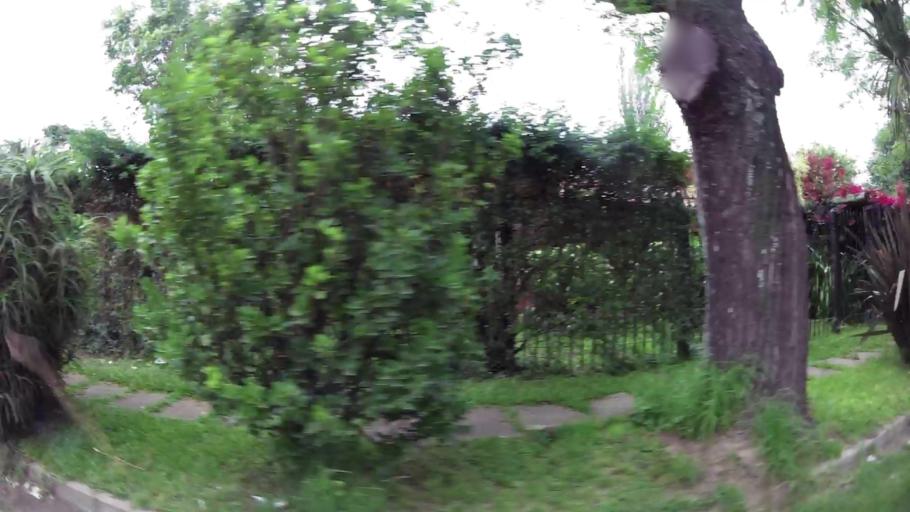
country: AR
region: Buenos Aires
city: San Justo
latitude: -34.7212
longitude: -58.5229
